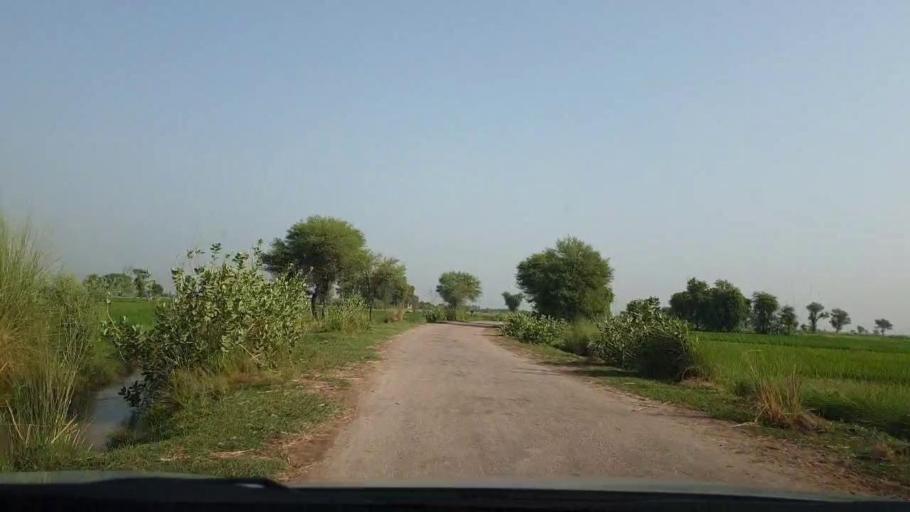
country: PK
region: Sindh
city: Goth Garelo
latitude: 27.4712
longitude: 68.1186
